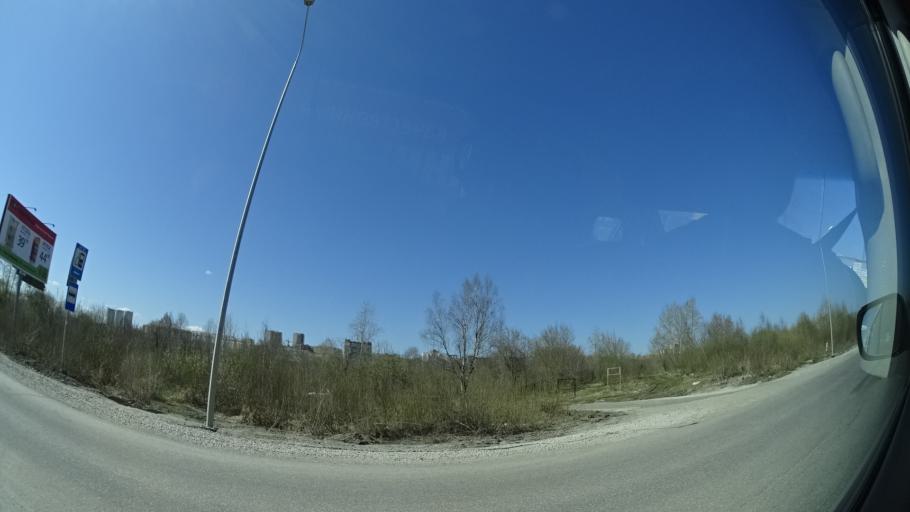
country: RU
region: Perm
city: Perm
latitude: 58.0977
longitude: 56.3193
